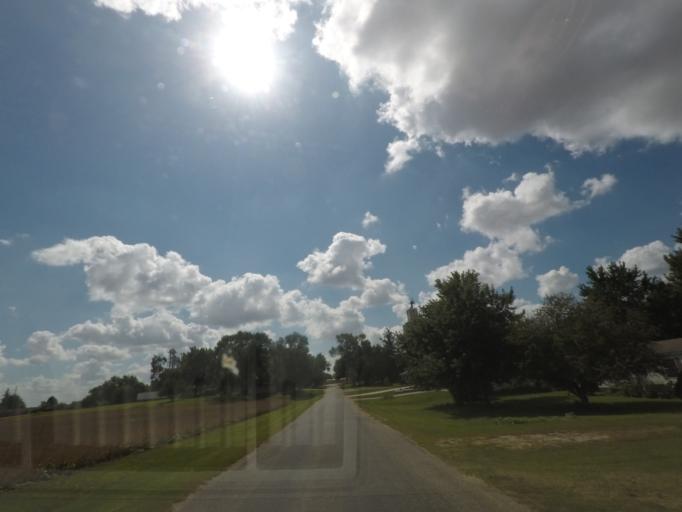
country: US
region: Iowa
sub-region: Story County
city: Nevada
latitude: 42.0212
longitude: -93.3127
